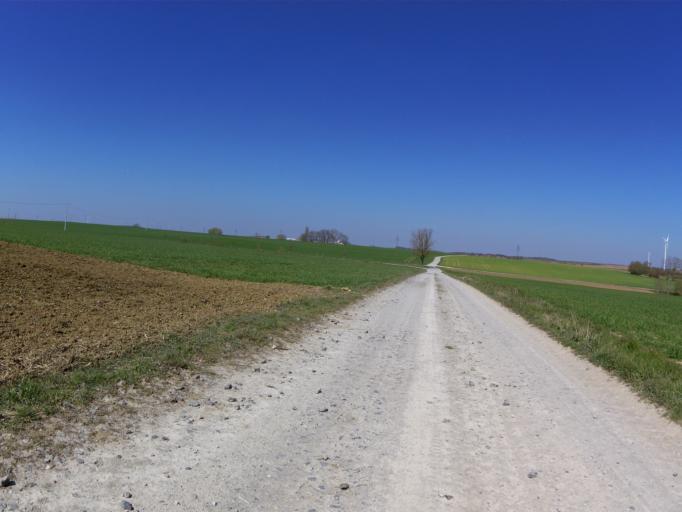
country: DE
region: Bavaria
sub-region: Regierungsbezirk Unterfranken
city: Biebelried
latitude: 49.7428
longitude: 10.0878
